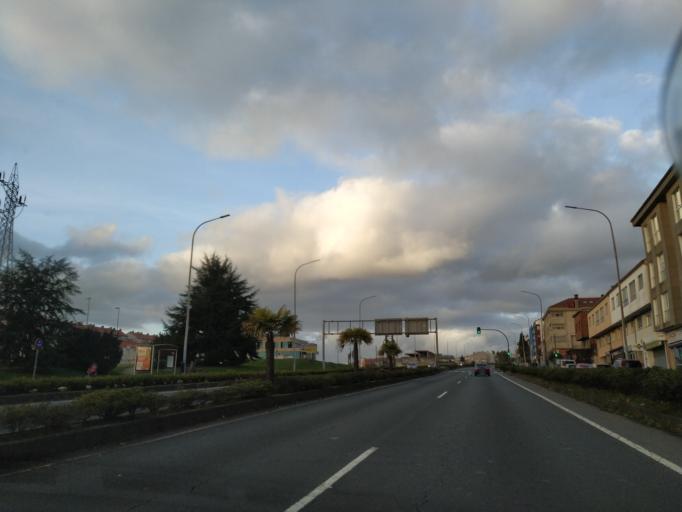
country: ES
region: Galicia
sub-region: Provincia da Coruna
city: Santiago de Compostela
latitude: 42.8931
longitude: -8.5325
